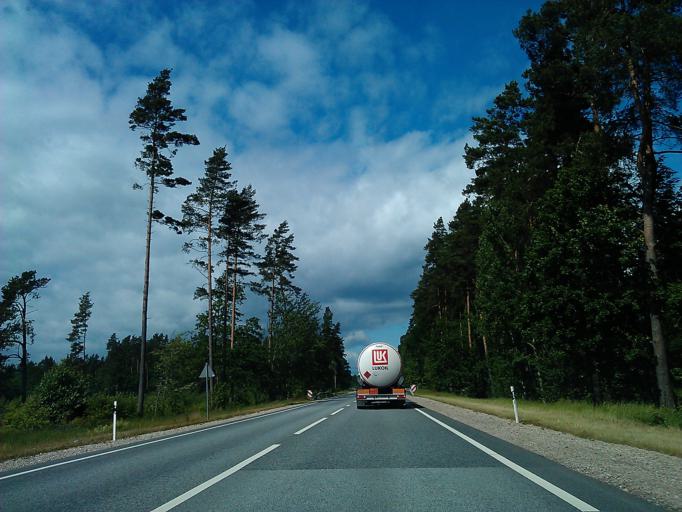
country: LV
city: Tireli
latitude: 56.9280
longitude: 23.6559
